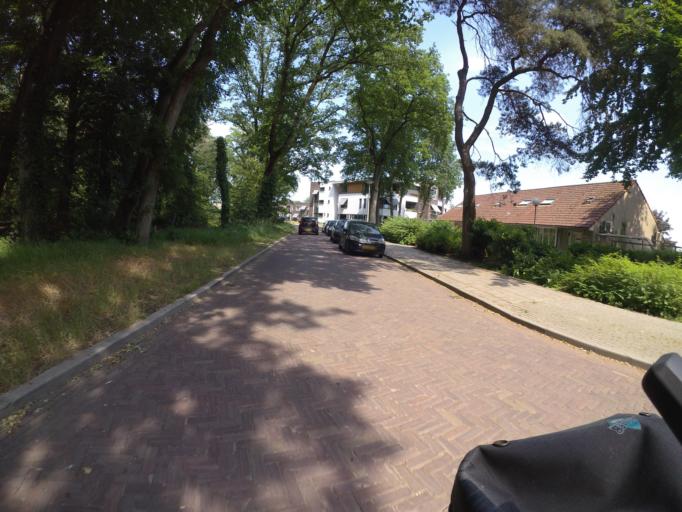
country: NL
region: Overijssel
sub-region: Gemeente Twenterand
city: Den Ham
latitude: 52.3611
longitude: 6.4483
